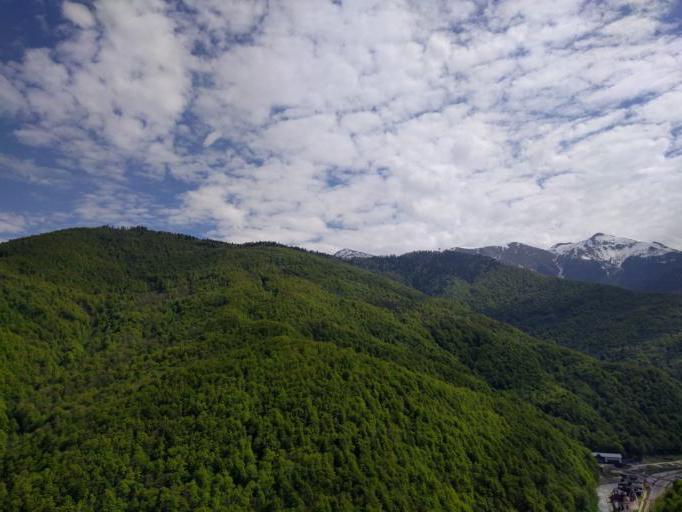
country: RU
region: Krasnodarskiy
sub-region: Sochi City
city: Krasnaya Polyana
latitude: 43.6694
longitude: 40.3020
